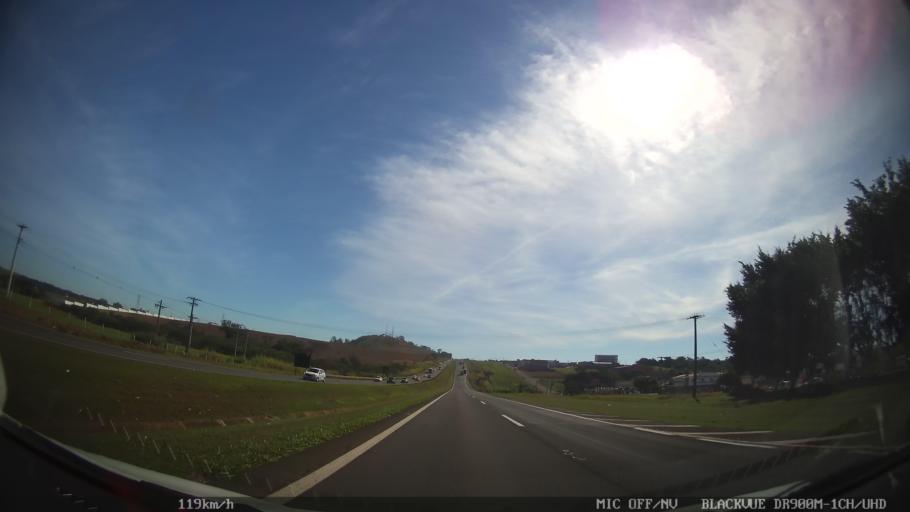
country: BR
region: Sao Paulo
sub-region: Leme
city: Leme
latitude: -22.1715
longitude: -47.3988
